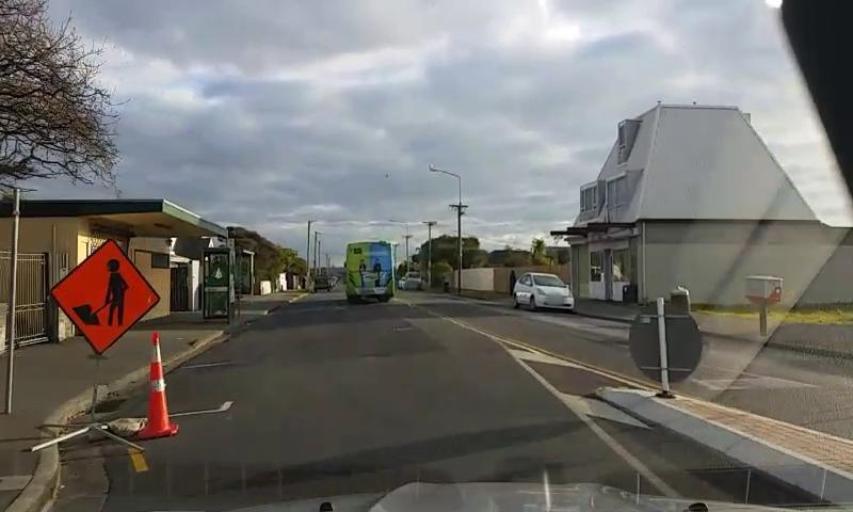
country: NZ
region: Canterbury
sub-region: Christchurch City
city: Christchurch
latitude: -43.5232
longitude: 172.7326
